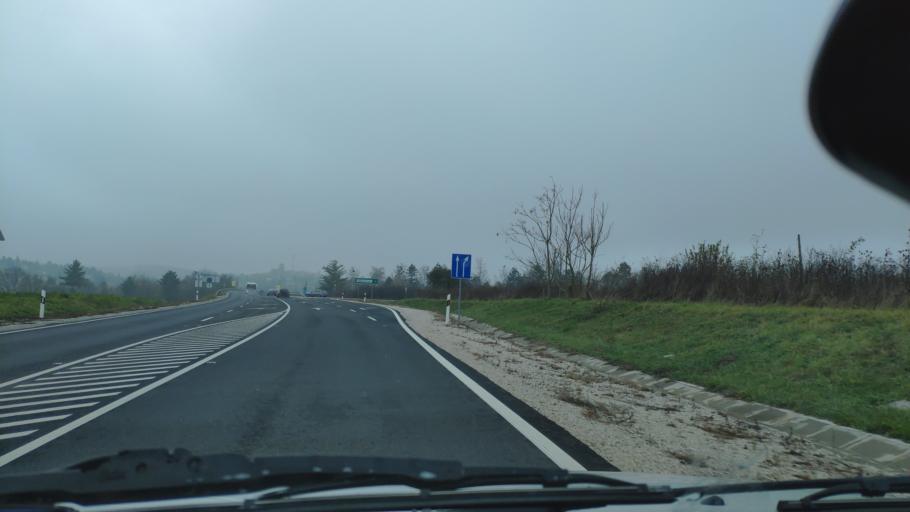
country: HU
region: Zala
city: Nagykanizsa
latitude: 46.4501
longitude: 17.0307
